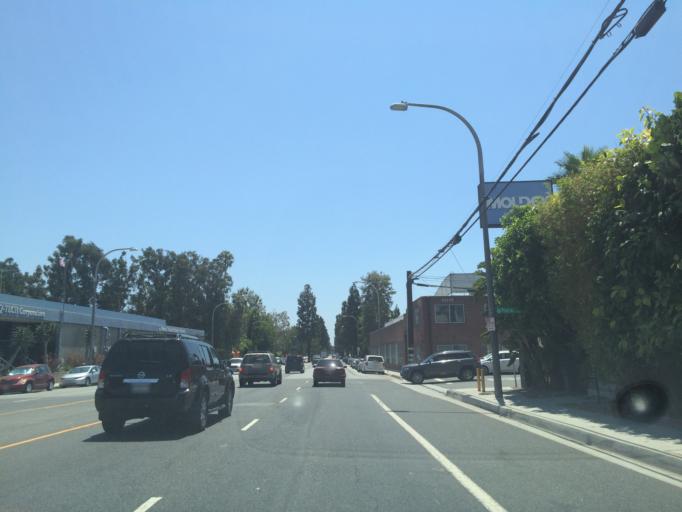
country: US
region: California
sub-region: Los Angeles County
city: Culver City
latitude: 34.0124
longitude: -118.3894
